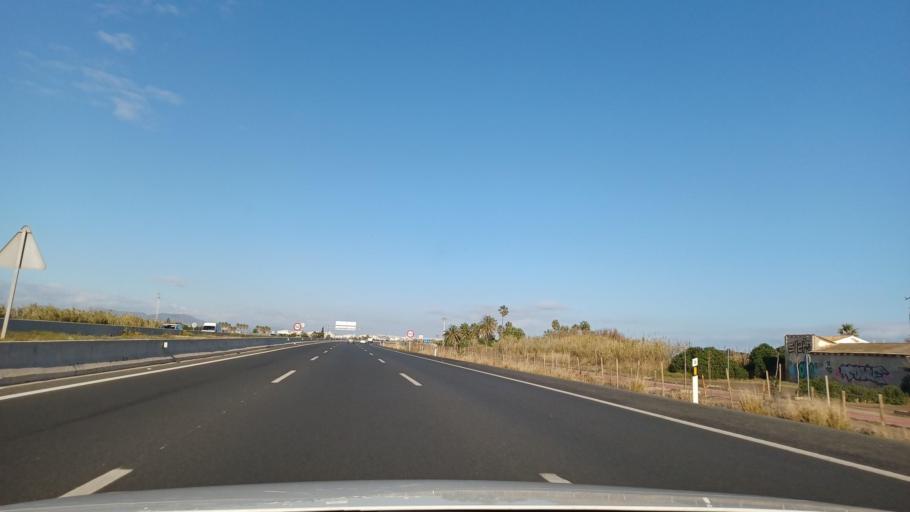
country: ES
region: Valencia
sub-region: Provincia de Valencia
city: Meliana
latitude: 39.5164
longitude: -0.3203
